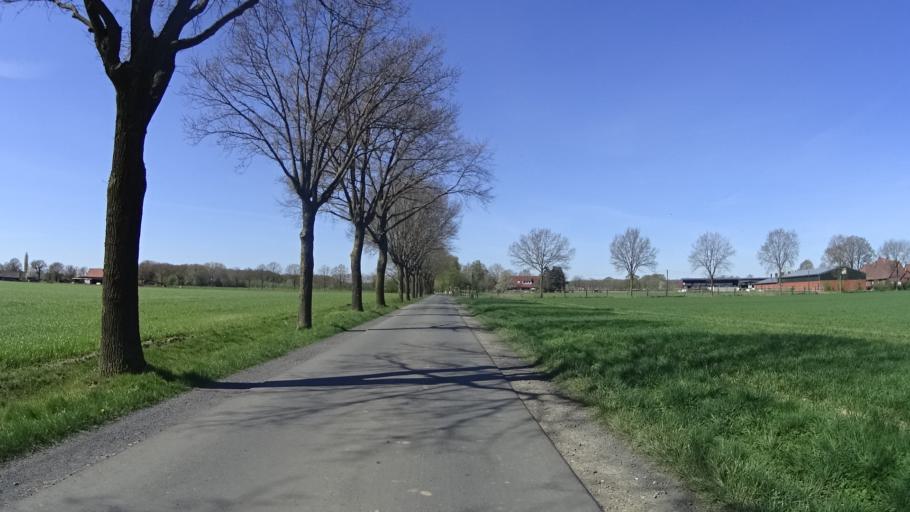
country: DE
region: North Rhine-Westphalia
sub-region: Regierungsbezirk Munster
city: Senden
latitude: 51.9046
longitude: 7.5368
